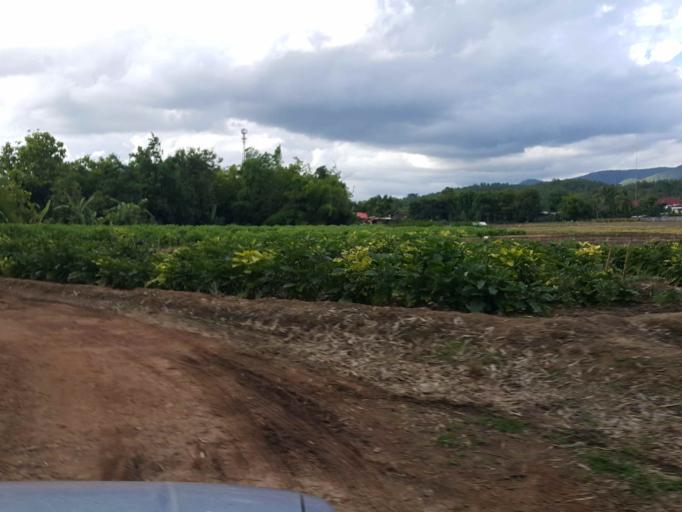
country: TH
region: Chiang Mai
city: Mae Chaem
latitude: 18.4949
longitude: 98.3660
